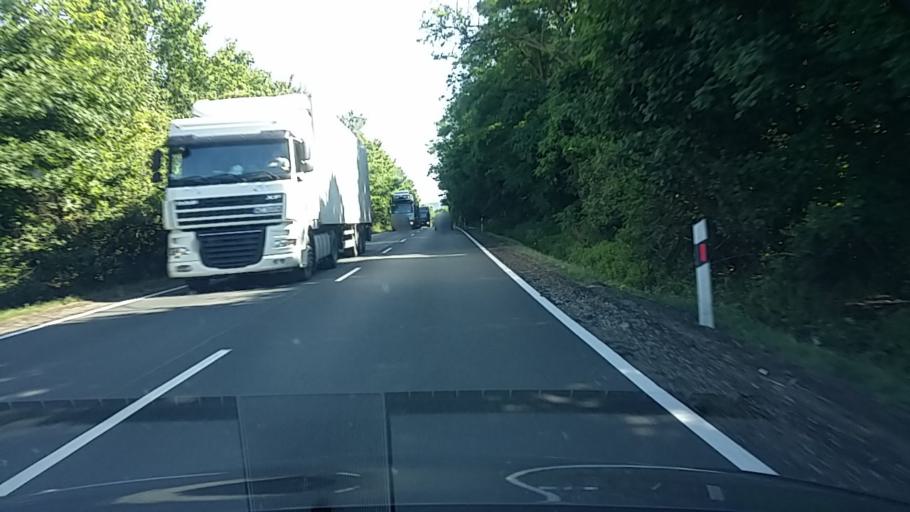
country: HU
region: Nograd
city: Retsag
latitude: 47.8792
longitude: 19.1046
